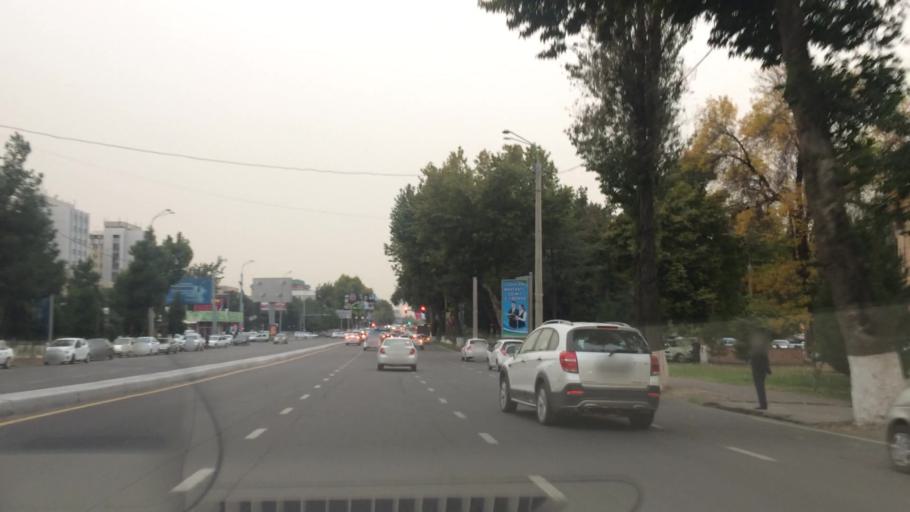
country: UZ
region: Toshkent Shahri
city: Tashkent
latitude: 41.3043
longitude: 69.2810
